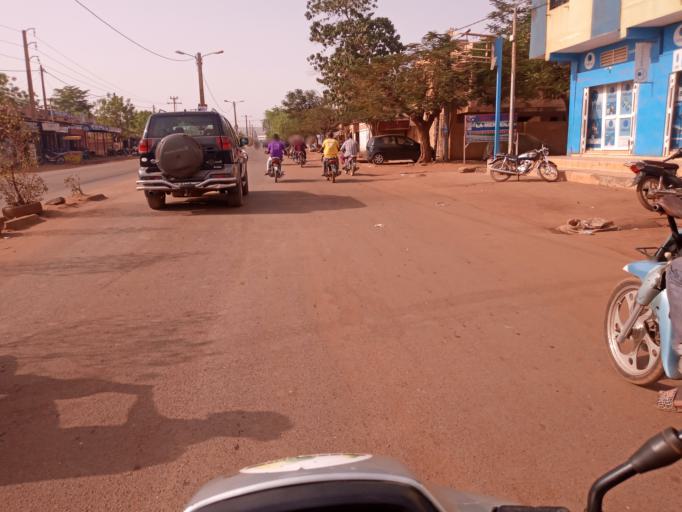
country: ML
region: Bamako
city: Bamako
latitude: 12.6731
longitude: -7.9431
